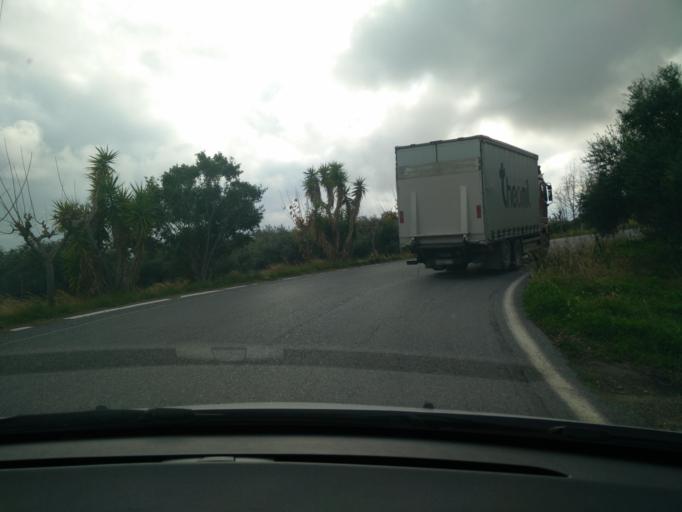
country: GR
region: Crete
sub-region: Nomos Lasithiou
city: Gra Liyia
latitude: 35.0253
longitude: 25.5679
